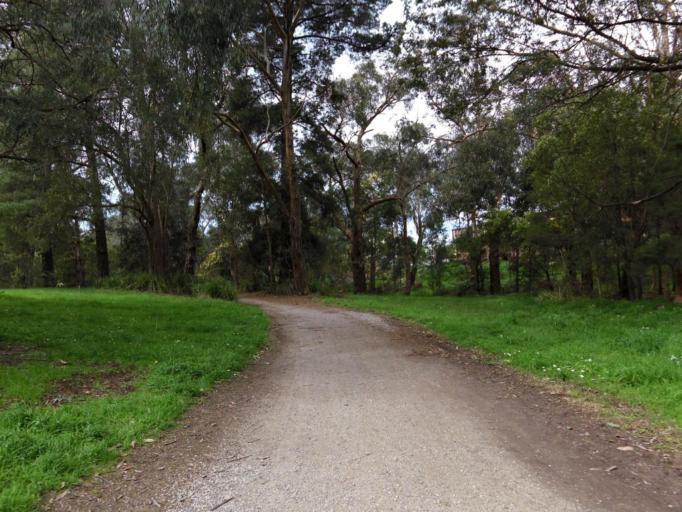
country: AU
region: Victoria
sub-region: Maroondah
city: Ringwood East
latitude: -37.8018
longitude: 145.2455
